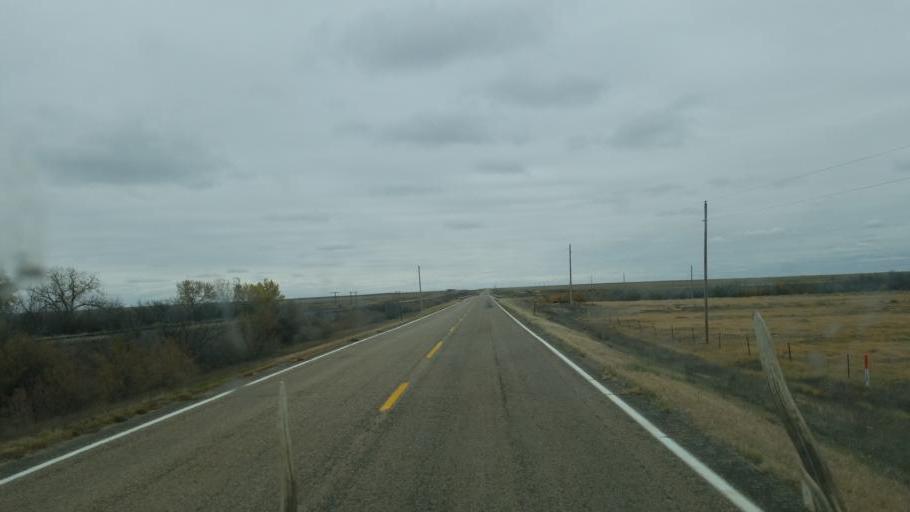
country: US
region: Colorado
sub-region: Crowley County
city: Ordway
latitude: 38.2387
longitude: -103.6380
